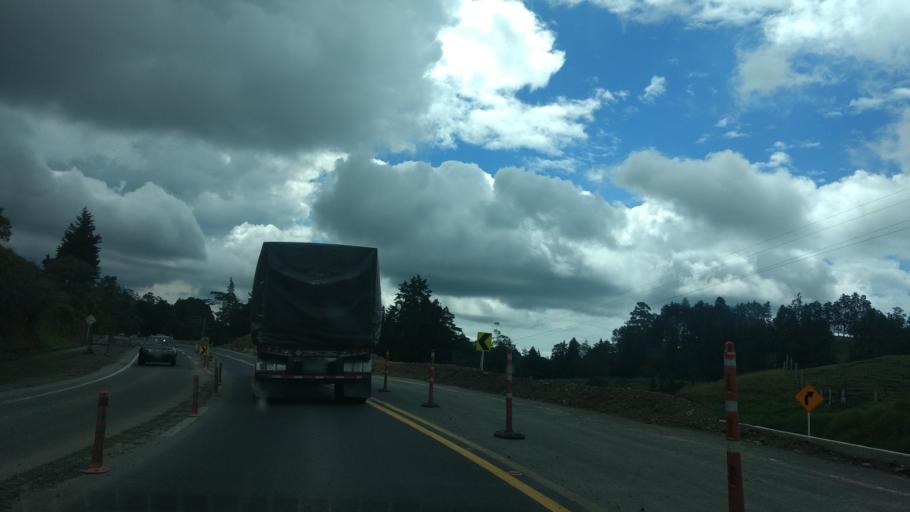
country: CO
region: Cundinamarca
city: San Francisco
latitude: 4.9310
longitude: -74.2971
